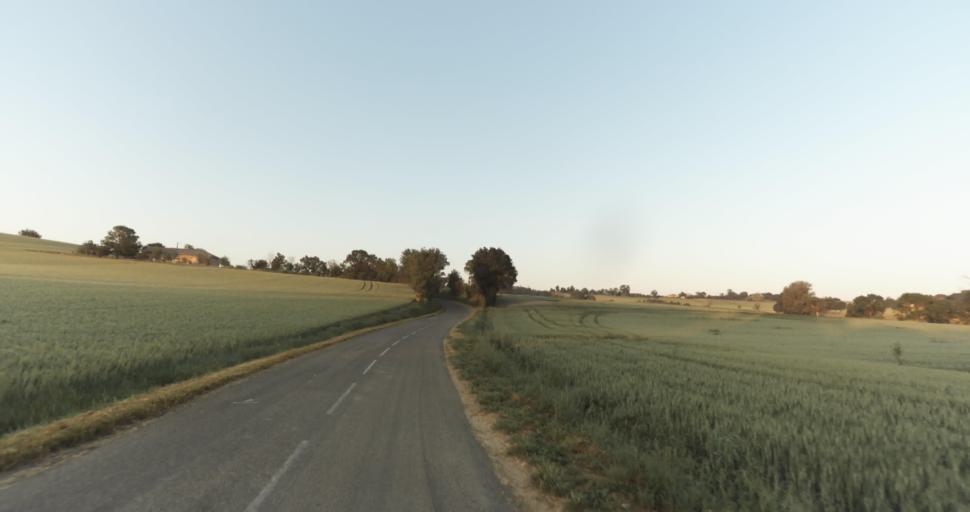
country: FR
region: Midi-Pyrenees
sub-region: Departement du Gers
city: Pujaudran
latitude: 43.6567
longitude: 1.1095
